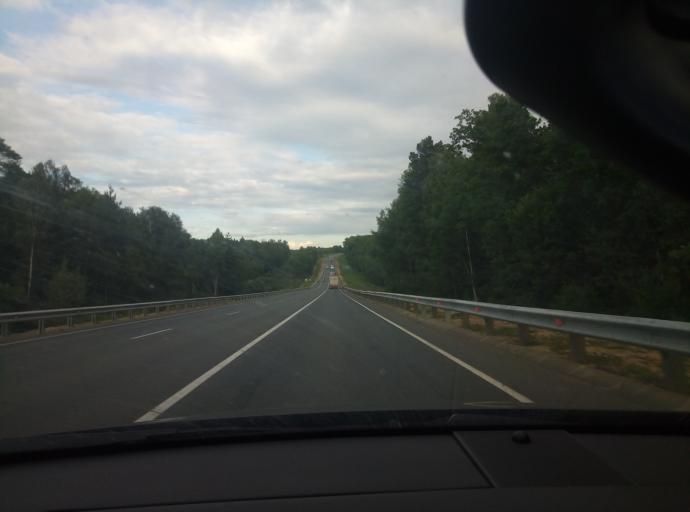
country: RU
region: Tula
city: Dubna
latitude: 54.3213
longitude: 36.9759
